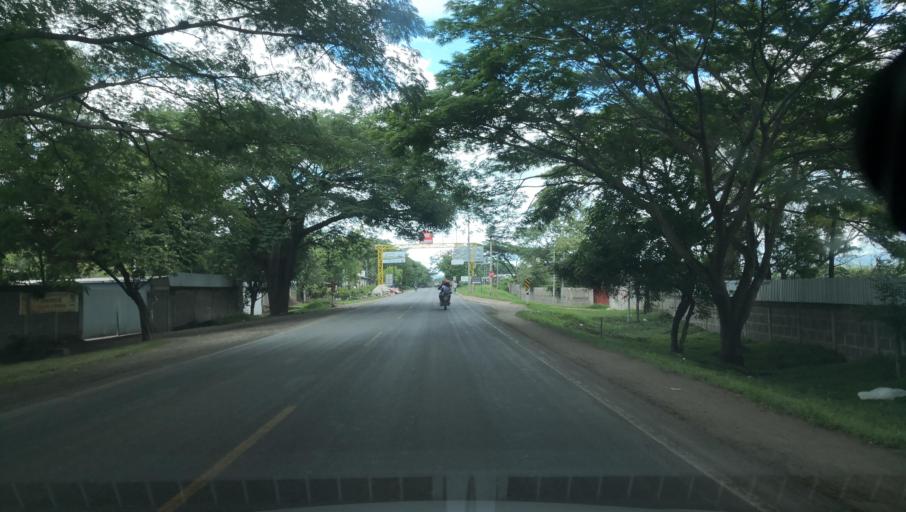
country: NI
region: Esteli
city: Esteli
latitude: 13.1203
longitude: -86.3626
